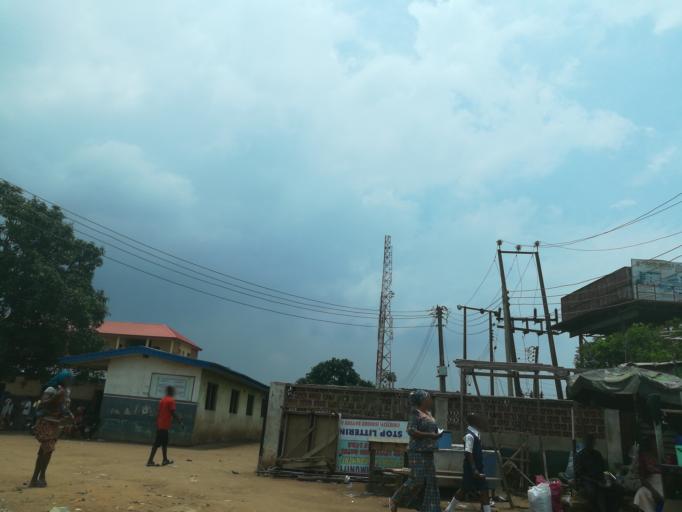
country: NG
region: Lagos
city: Ikorodu
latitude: 6.6161
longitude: 3.5674
